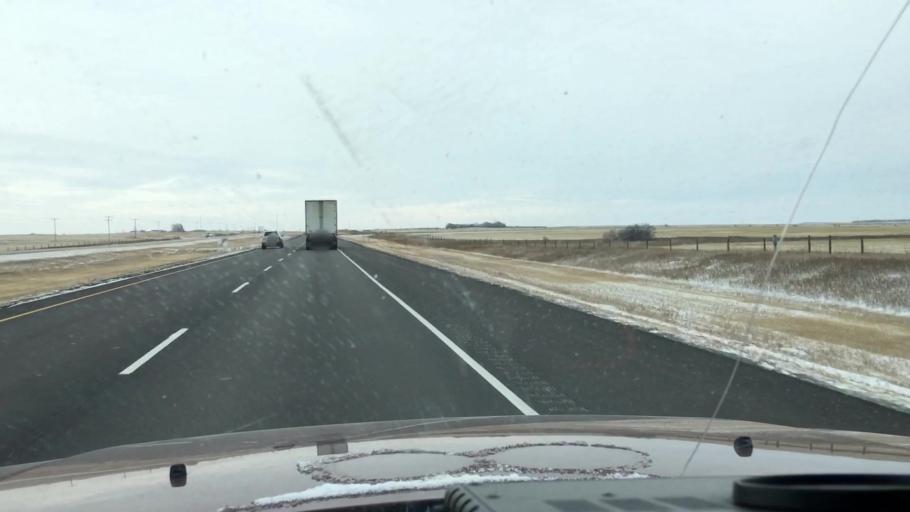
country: CA
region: Saskatchewan
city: Saskatoon
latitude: 51.7978
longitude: -106.4881
